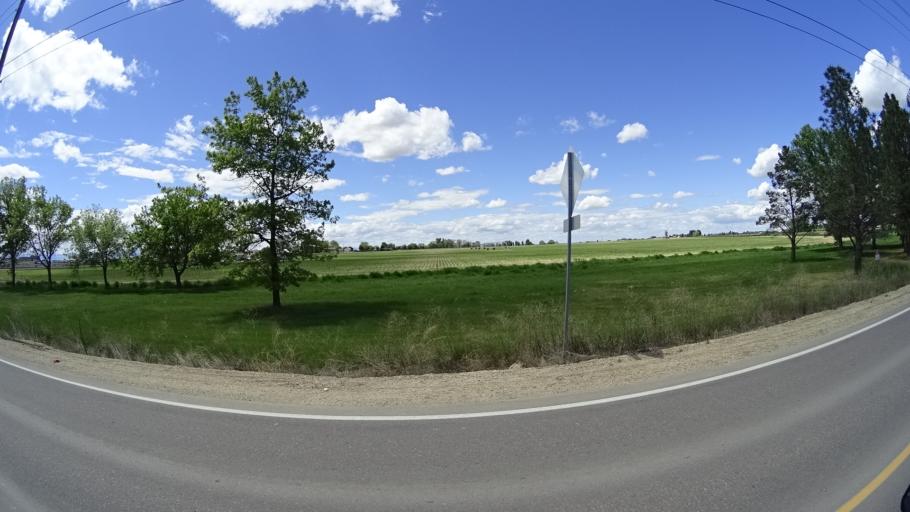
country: US
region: Idaho
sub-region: Ada County
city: Kuna
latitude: 43.5479
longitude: -116.4338
